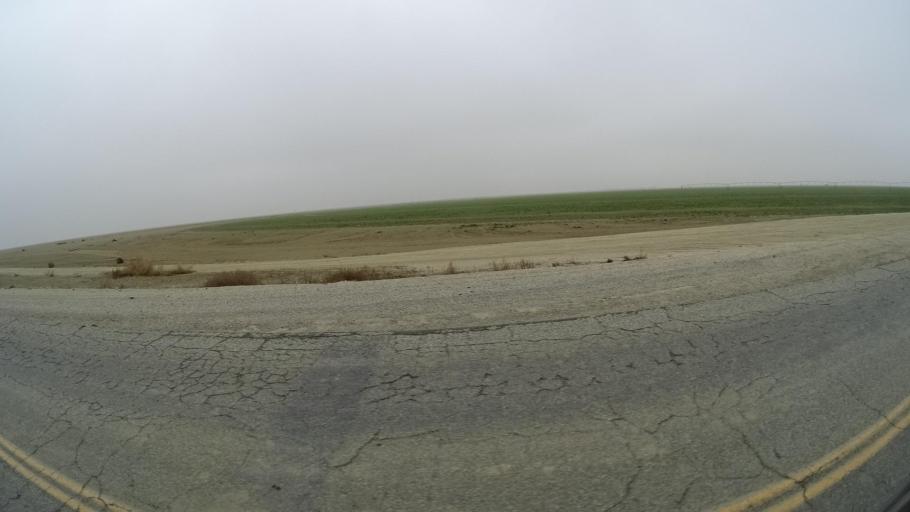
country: US
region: California
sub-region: Kern County
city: Maricopa
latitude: 35.1522
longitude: -119.2019
